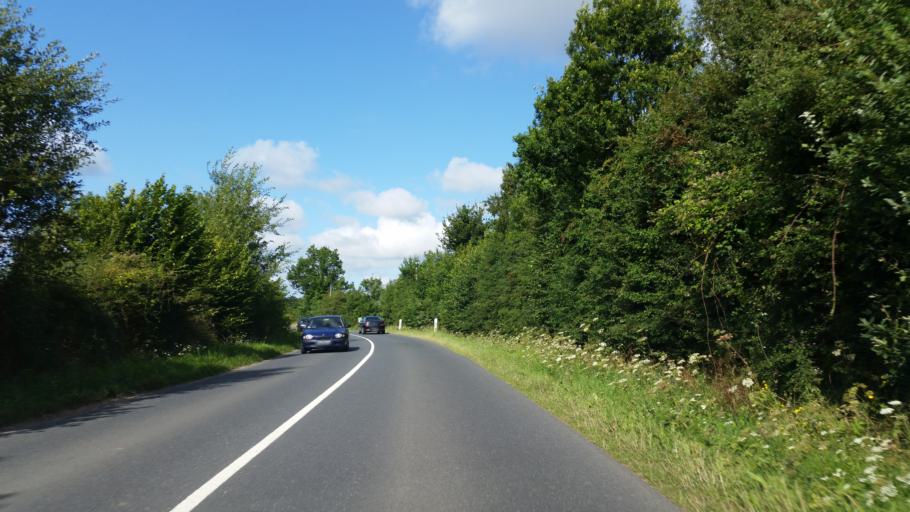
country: FR
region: Lower Normandy
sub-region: Departement du Calvados
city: Dozule
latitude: 49.2652
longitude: -0.0407
